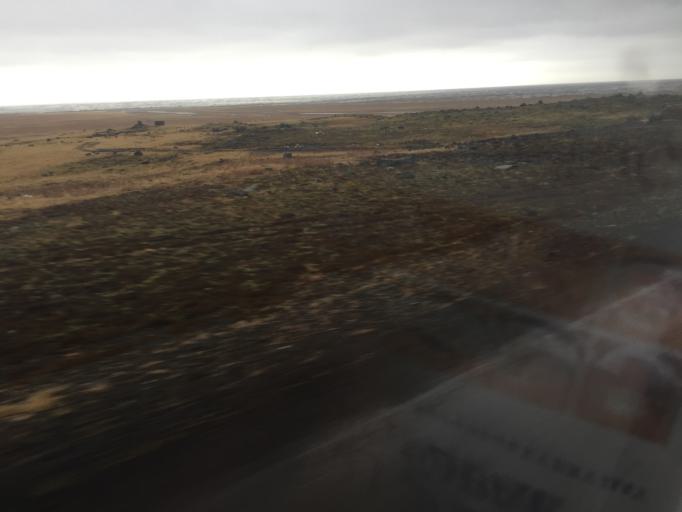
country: IS
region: East
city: Hoefn
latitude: 63.8809
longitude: -16.6790
